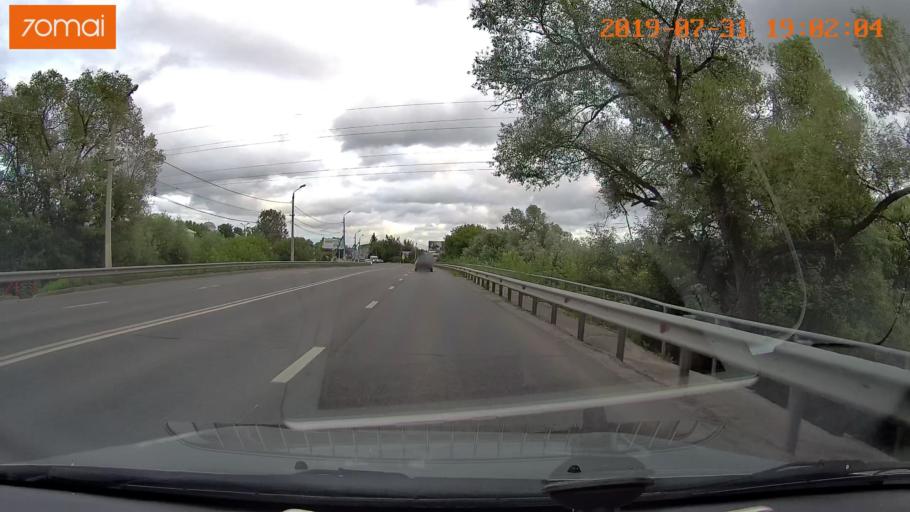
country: RU
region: Moskovskaya
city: Raduzhnyy
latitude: 55.1220
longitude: 38.7305
